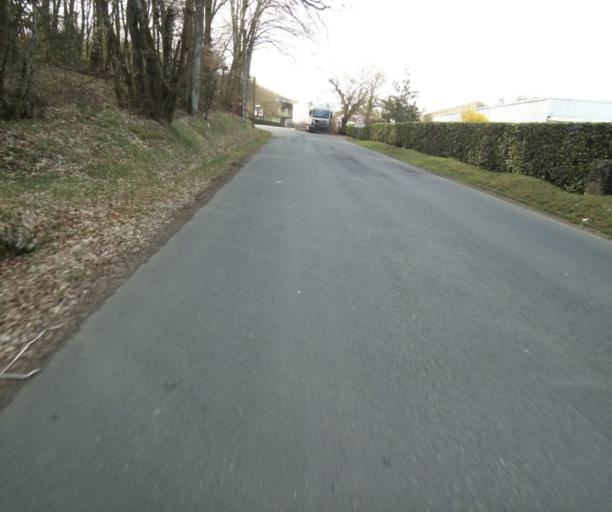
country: FR
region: Limousin
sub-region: Departement de la Correze
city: Tulle
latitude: 45.2856
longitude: 1.7645
